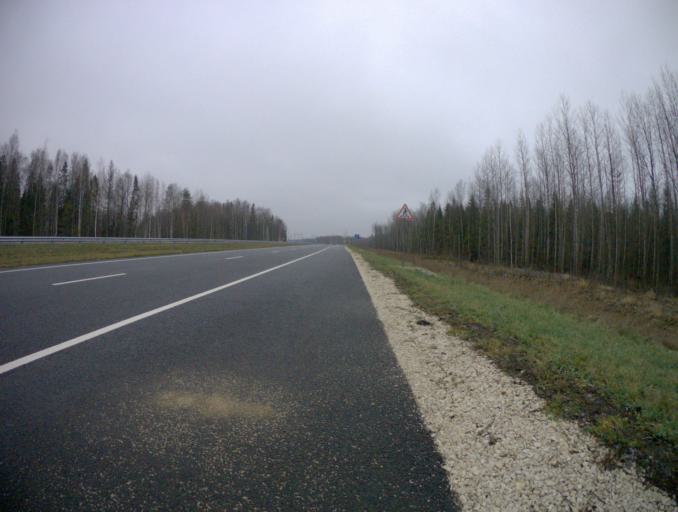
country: RU
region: Vladimir
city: Kommunar
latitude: 56.0435
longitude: 40.5213
